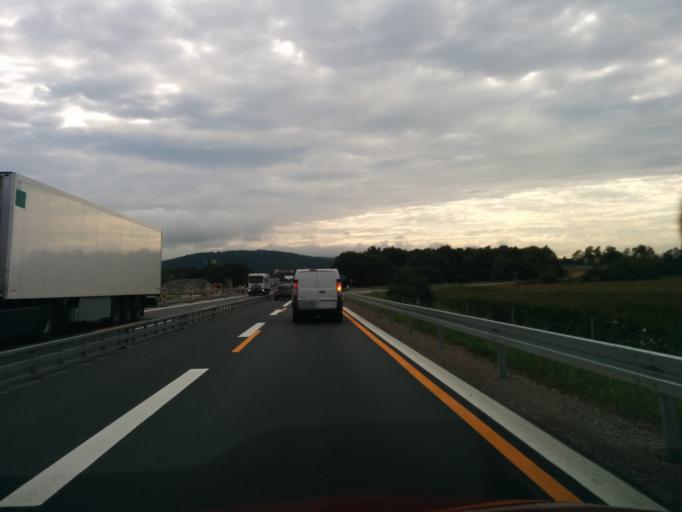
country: DE
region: Bavaria
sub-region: Upper Palatinate
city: Wiesent
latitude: 48.9994
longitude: 12.3584
